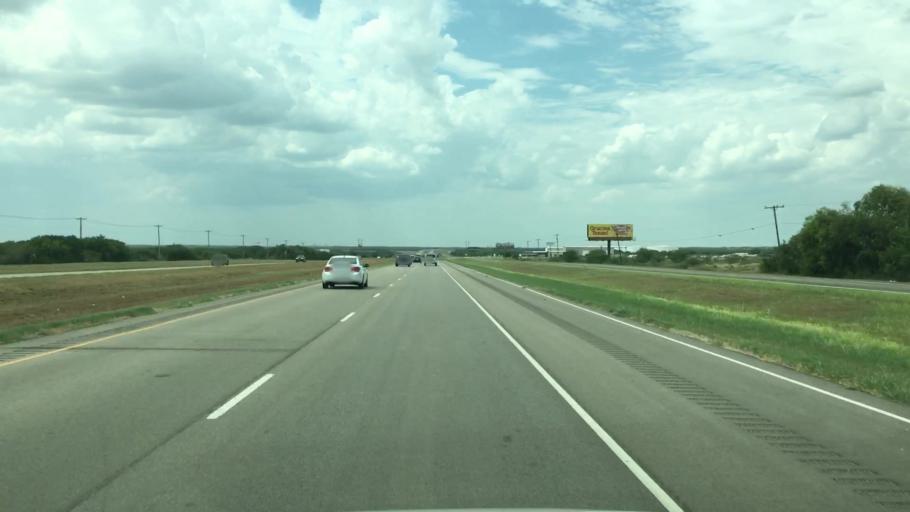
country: US
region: Texas
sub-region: Live Oak County
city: Three Rivers
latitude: 28.5058
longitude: -98.1624
